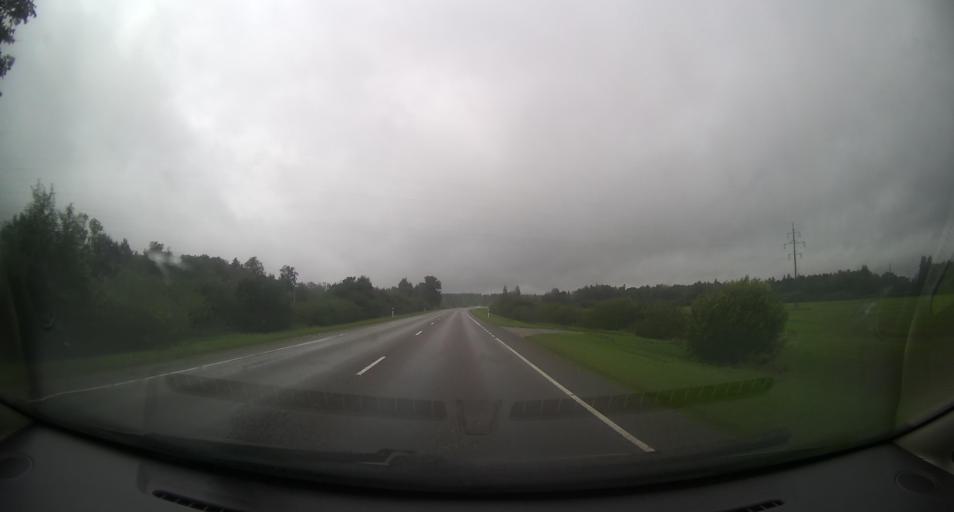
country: EE
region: Laeaene
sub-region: Lihula vald
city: Lihula
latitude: 58.6737
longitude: 23.7727
